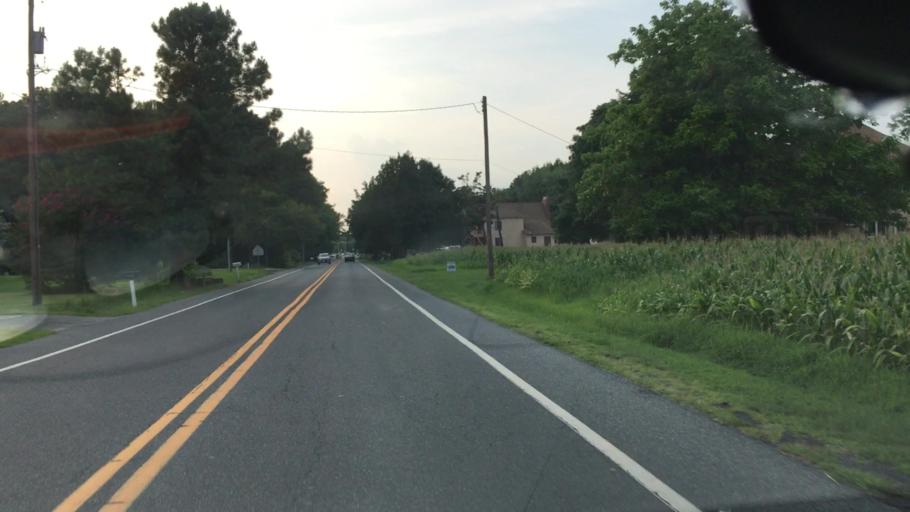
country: US
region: Delaware
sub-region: Sussex County
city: Ocean View
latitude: 38.5435
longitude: -75.1025
